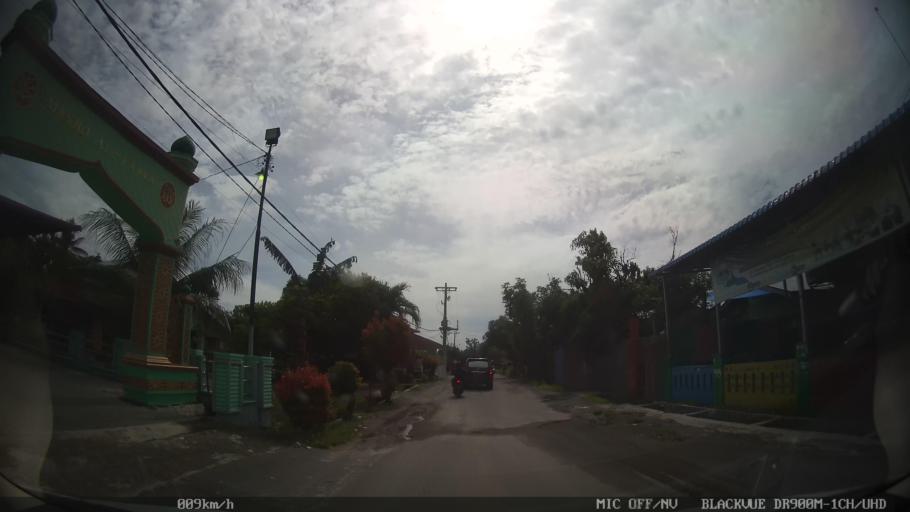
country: ID
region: North Sumatra
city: Percut
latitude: 3.6198
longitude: 98.7947
